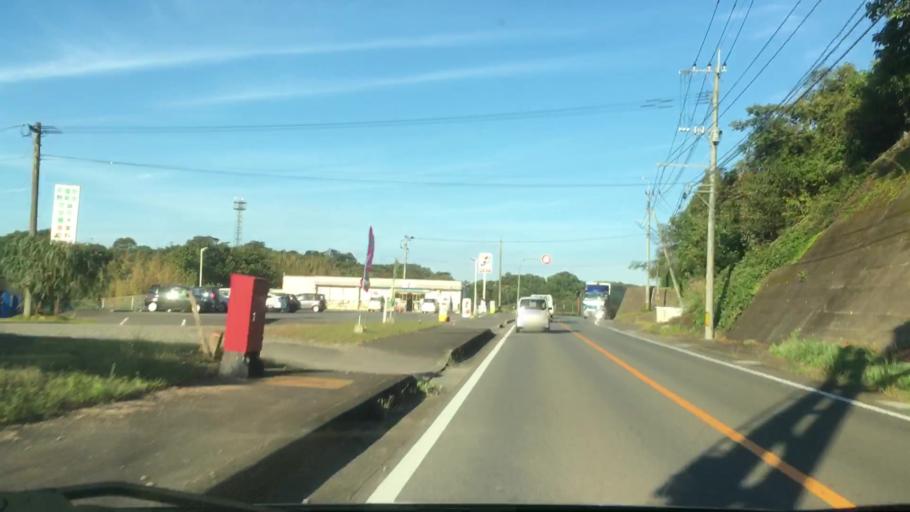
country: JP
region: Nagasaki
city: Sasebo
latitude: 33.0447
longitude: 129.7344
